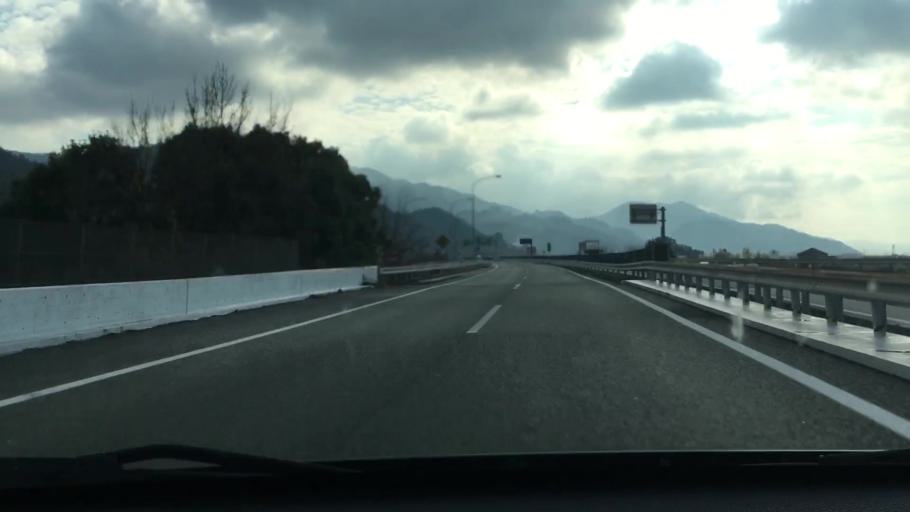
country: JP
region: Kumamoto
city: Yatsushiro
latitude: 32.5128
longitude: 130.6479
